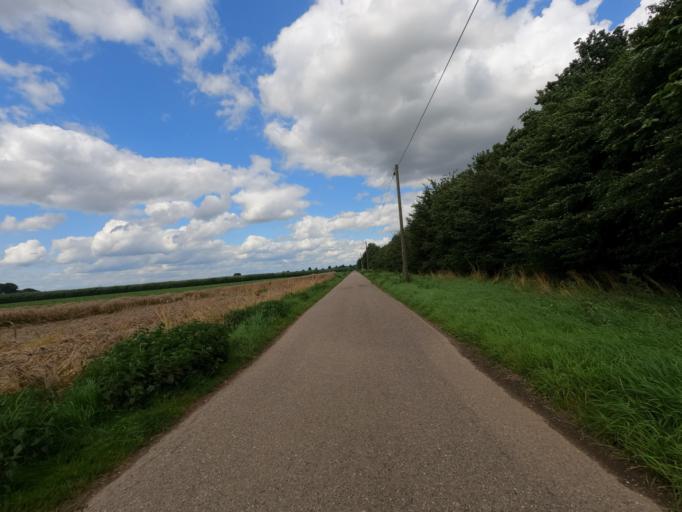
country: DE
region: North Rhine-Westphalia
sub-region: Regierungsbezirk Koln
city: Linnich
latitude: 50.9912
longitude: 6.2694
